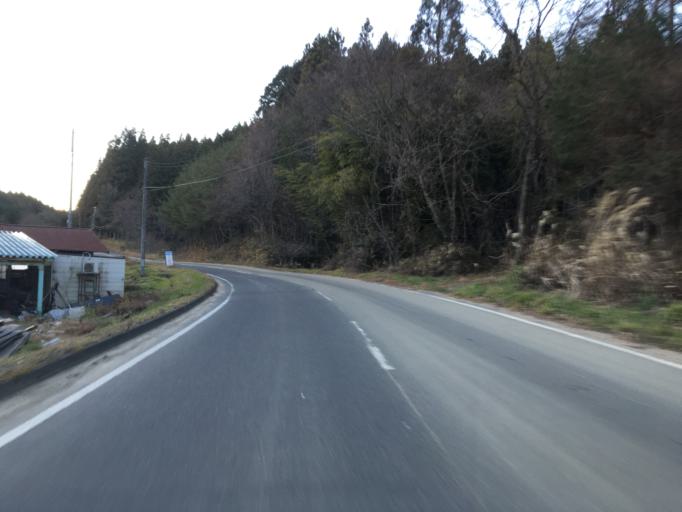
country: JP
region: Fukushima
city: Ishikawa
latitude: 37.2743
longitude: 140.5643
